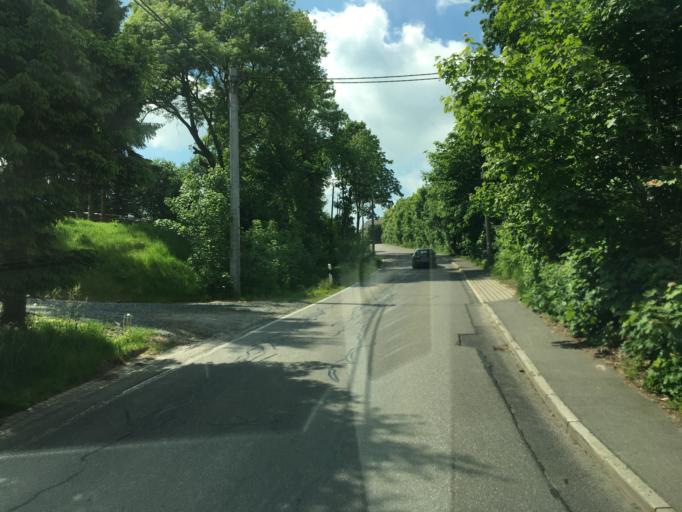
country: DE
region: Saxony
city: Oberschona
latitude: 50.9245
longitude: 13.2986
